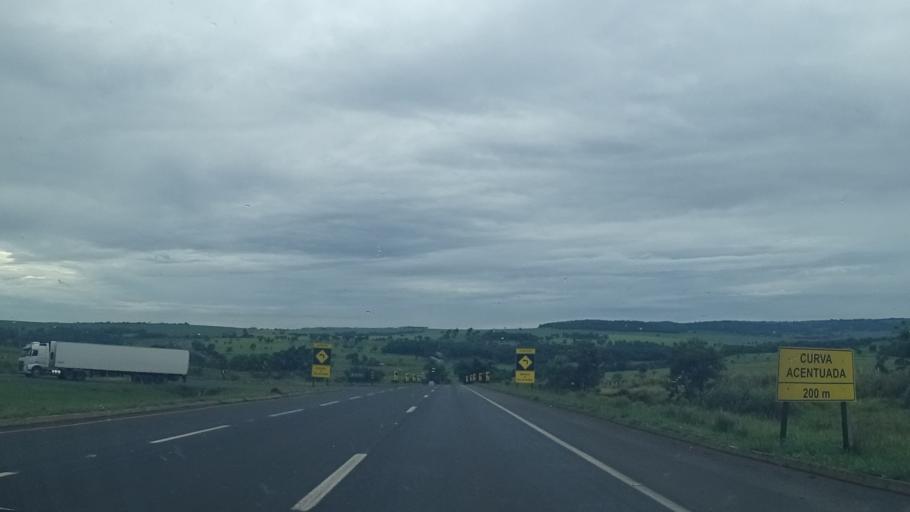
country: BR
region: Goias
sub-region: Goiatuba
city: Goiatuba
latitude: -18.1368
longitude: -49.2876
